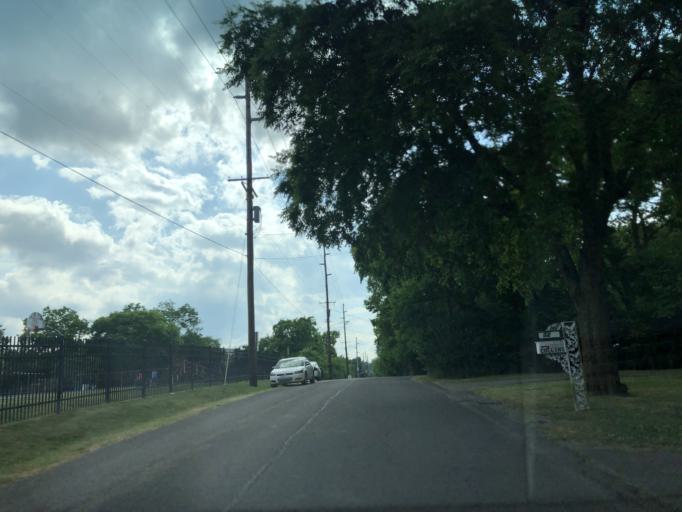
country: US
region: Tennessee
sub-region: Davidson County
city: Goodlettsville
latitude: 36.2748
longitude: -86.7042
